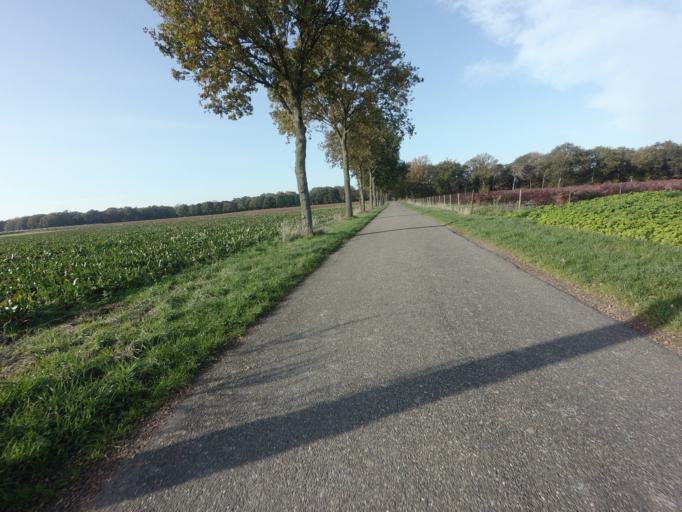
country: NL
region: Limburg
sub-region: Gemeente Echt-Susteren
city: Koningsbosch
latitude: 51.0567
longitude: 5.9318
